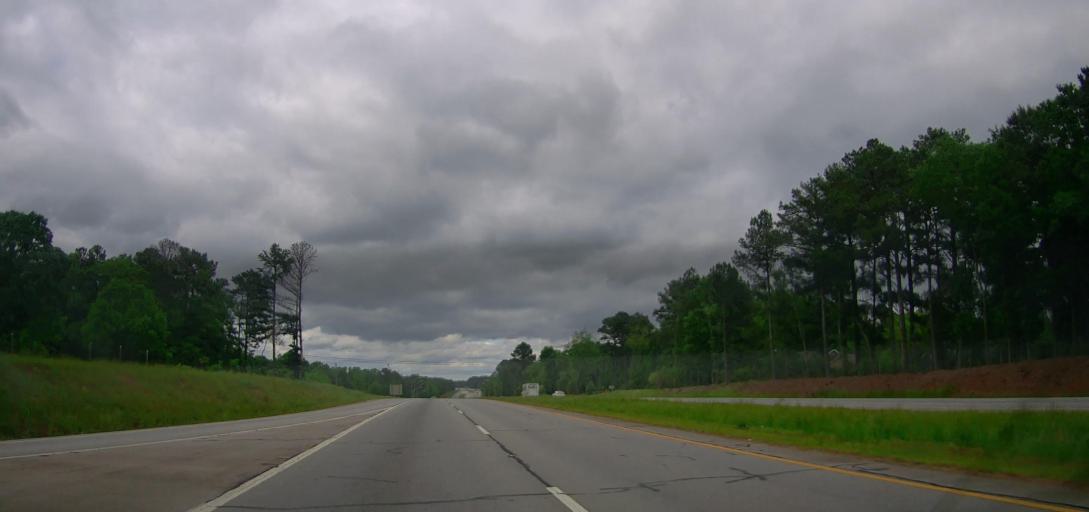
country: US
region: Georgia
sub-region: Walton County
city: Monroe
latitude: 33.8066
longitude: -83.6929
